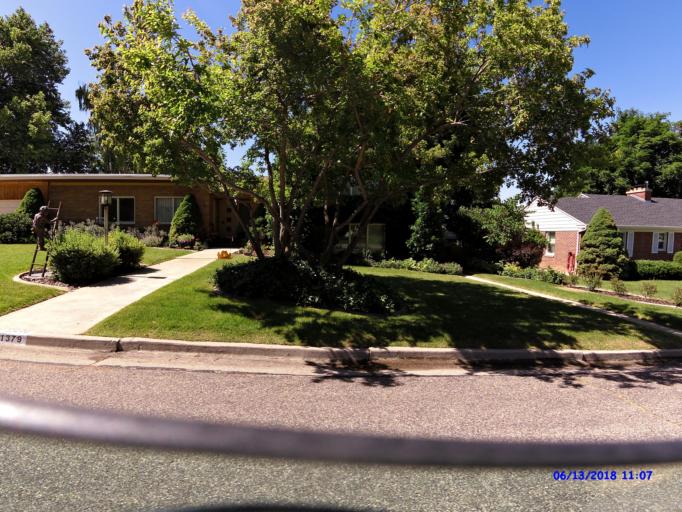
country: US
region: Utah
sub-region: Weber County
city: South Ogden
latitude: 41.2072
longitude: -111.9427
